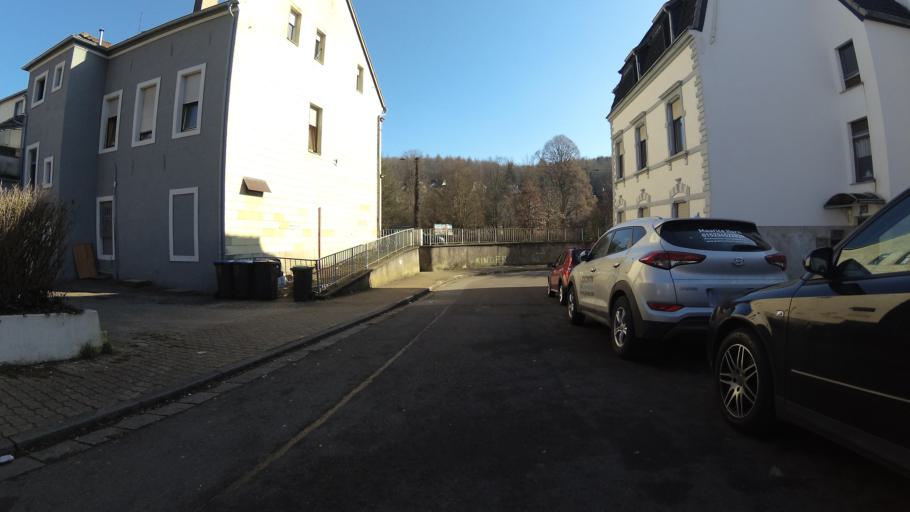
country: DE
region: Saarland
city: Sulzbach
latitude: 49.2947
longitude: 7.0520
